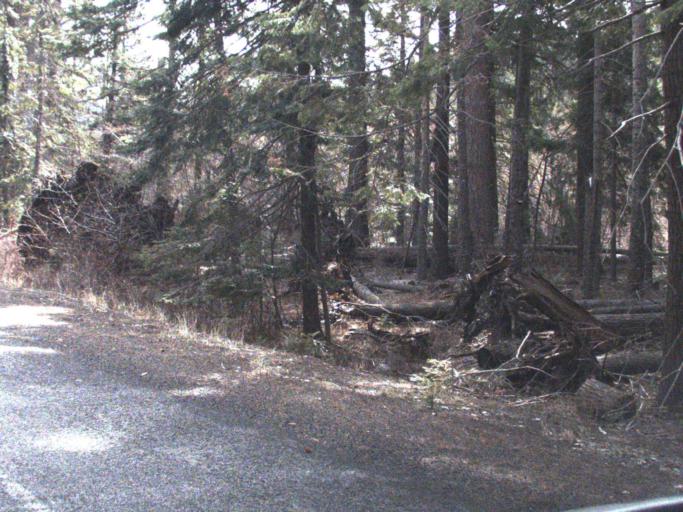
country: US
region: Washington
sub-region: Kittitas County
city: Cle Elum
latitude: 46.9677
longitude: -121.0900
